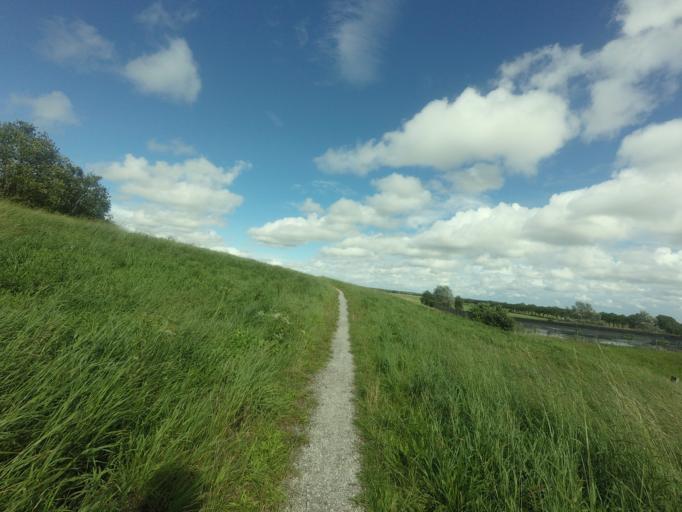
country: NL
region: Groningen
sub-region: Gemeente Leek
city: Leek
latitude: 53.0109
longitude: 6.3413
